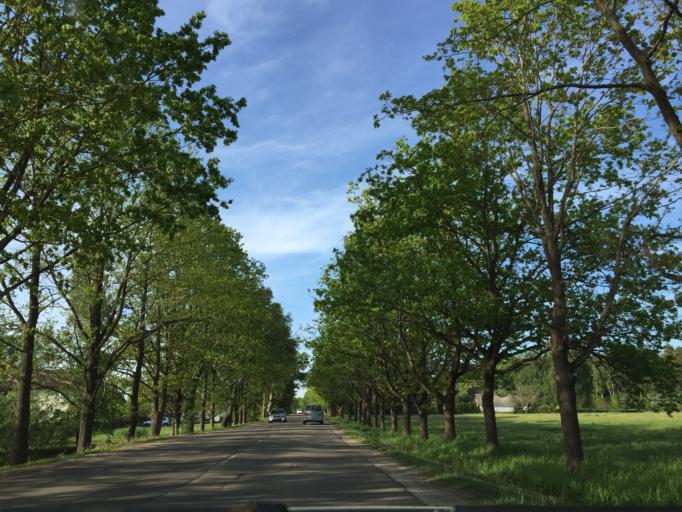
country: LV
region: Jelgava
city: Jelgava
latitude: 56.6134
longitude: 23.6851
